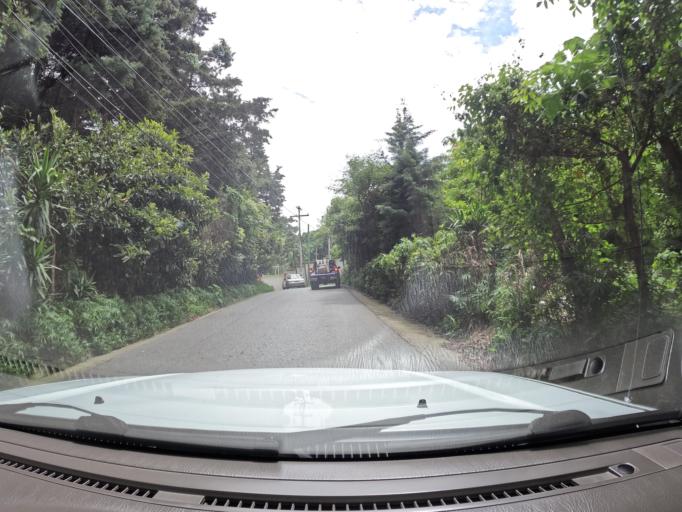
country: GT
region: Guatemala
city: Villa Canales
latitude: 14.4769
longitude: -90.4897
